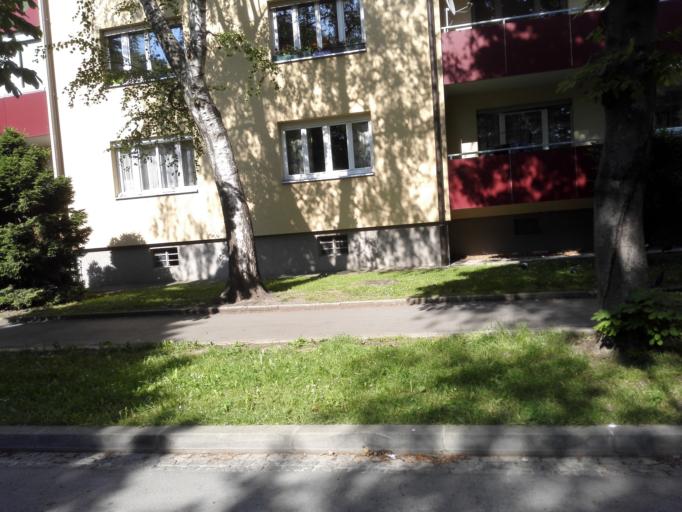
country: AT
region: Styria
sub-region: Graz Stadt
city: Goesting
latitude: 47.0775
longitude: 15.4122
